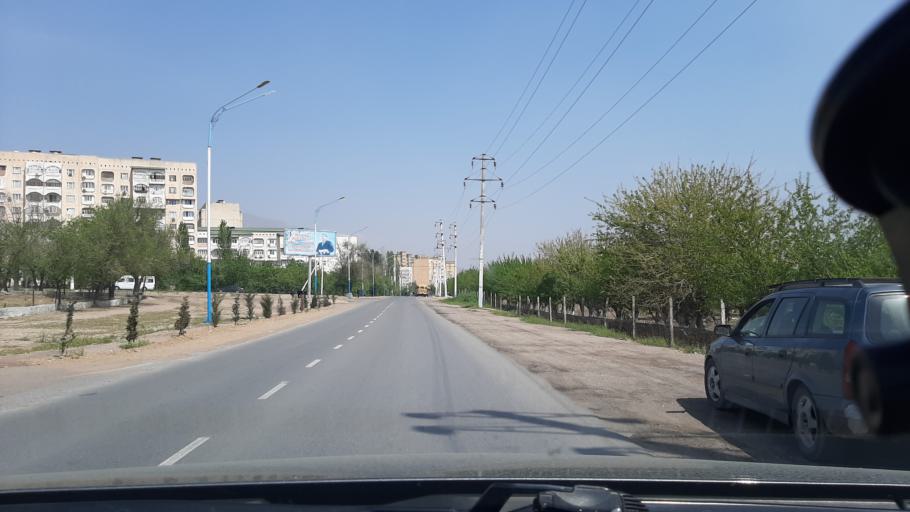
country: TJ
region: Viloyati Sughd
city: Khujand
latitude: 40.2844
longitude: 69.5889
